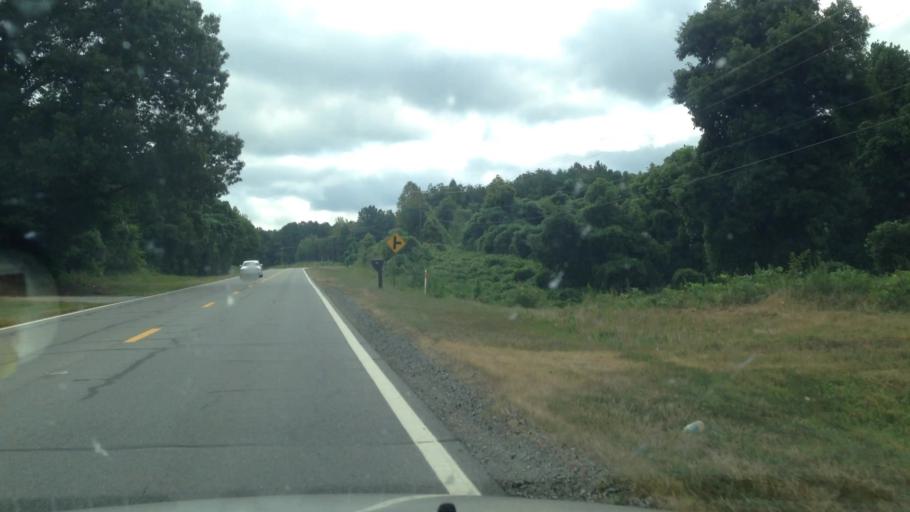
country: US
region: North Carolina
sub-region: Rockingham County
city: Wentworth
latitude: 36.3770
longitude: -79.8413
